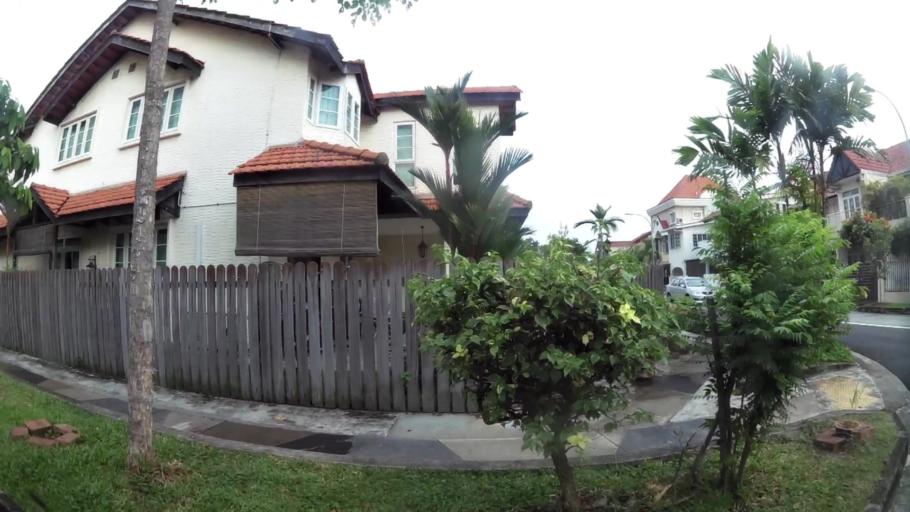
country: SG
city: Singapore
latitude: 1.3101
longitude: 103.9205
